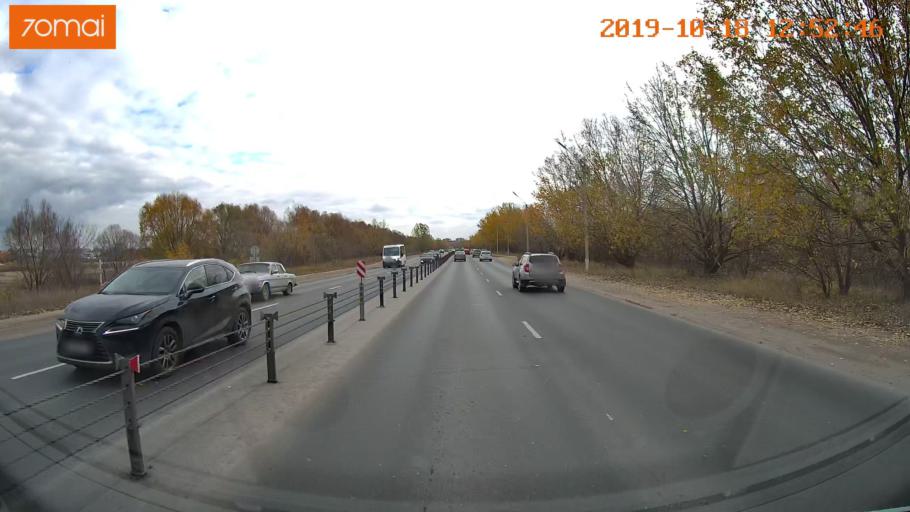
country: RU
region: Rjazan
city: Ryazan'
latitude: 54.6496
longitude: 39.6980
